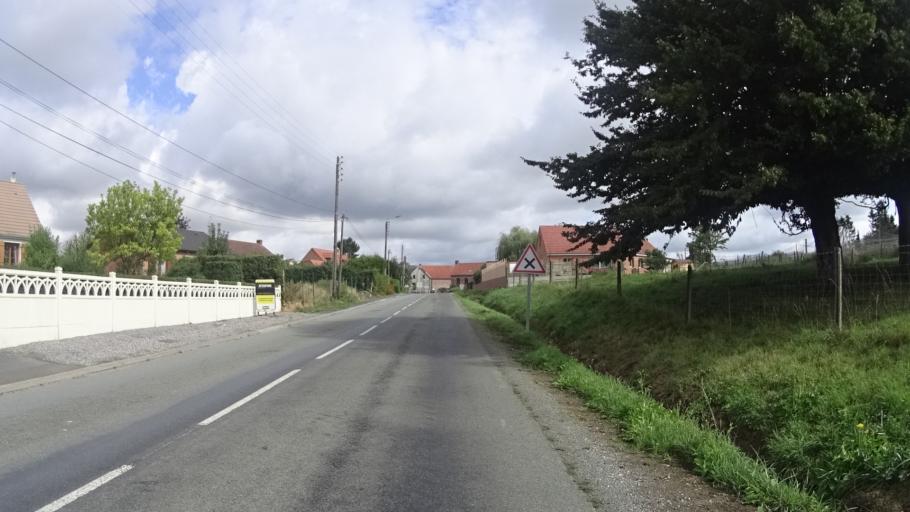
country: FR
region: Nord-Pas-de-Calais
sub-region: Departement du Nord
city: Bousies
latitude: 50.0970
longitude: 3.6390
